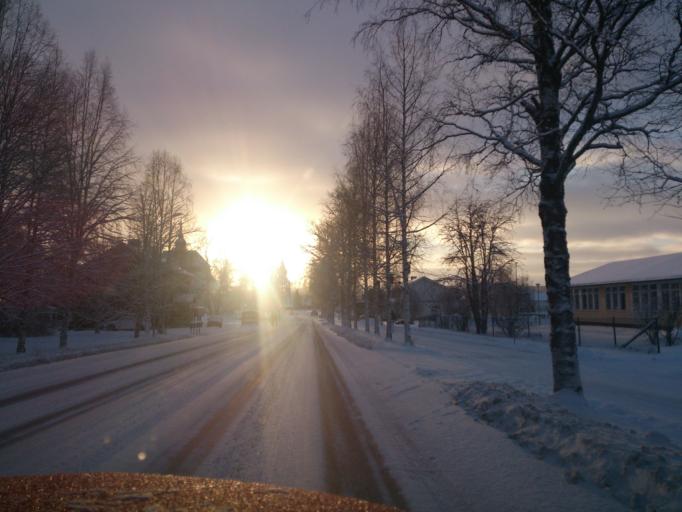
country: SE
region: Jaemtland
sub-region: Harjedalens Kommun
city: Sveg
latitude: 62.4473
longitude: 13.8626
